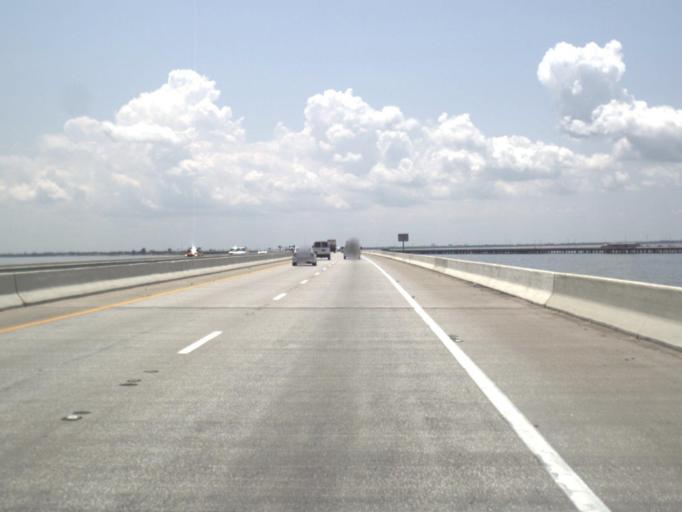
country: US
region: Florida
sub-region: Manatee County
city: West Bradenton
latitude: 27.6075
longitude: -82.6463
